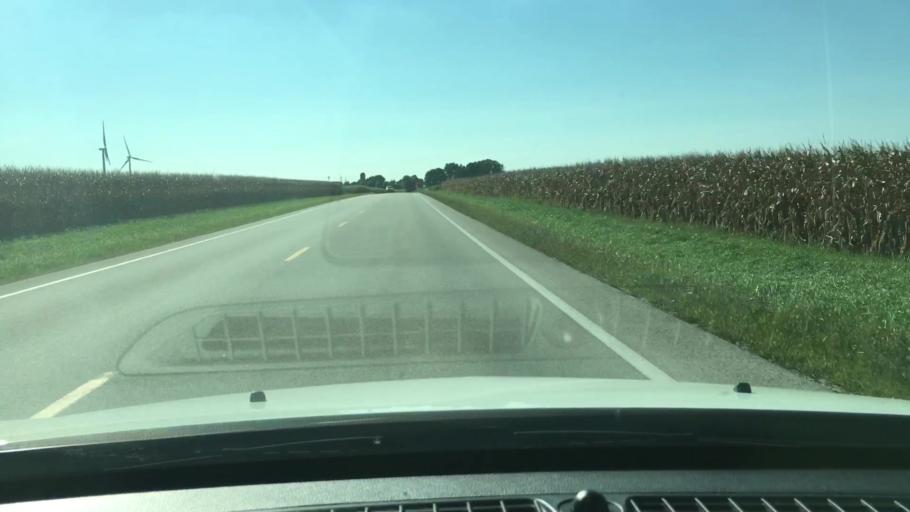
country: US
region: Illinois
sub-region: DeKalb County
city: Malta
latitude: 41.8494
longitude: -88.8643
